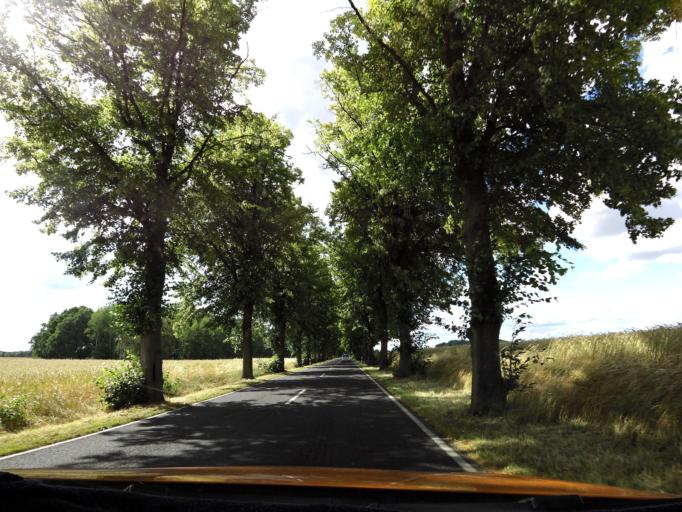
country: DE
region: Brandenburg
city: Mittenwalde
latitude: 52.2980
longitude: 13.5288
